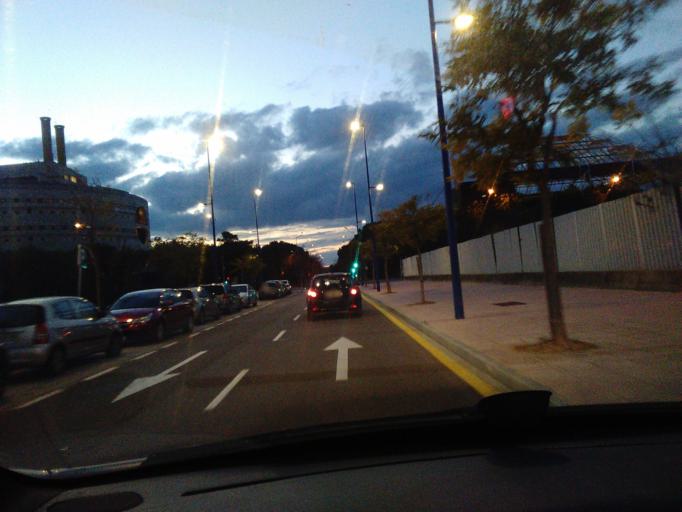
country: ES
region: Andalusia
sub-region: Provincia de Sevilla
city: Camas
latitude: 37.3942
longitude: -6.0092
